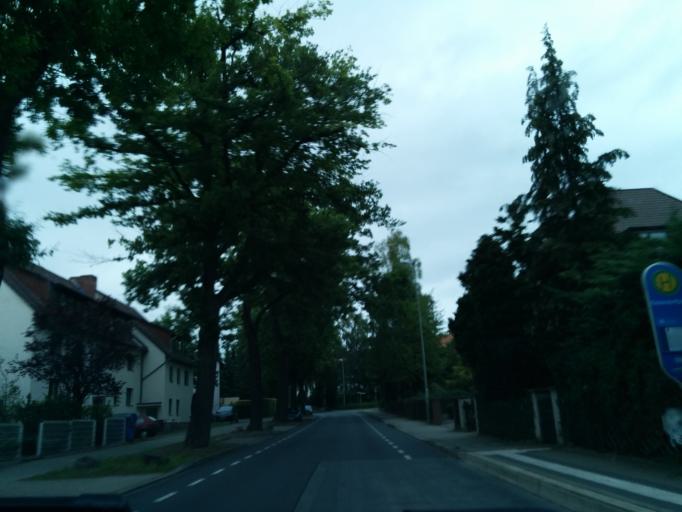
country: DE
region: Lower Saxony
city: Goettingen
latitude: 51.5397
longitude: 9.9494
